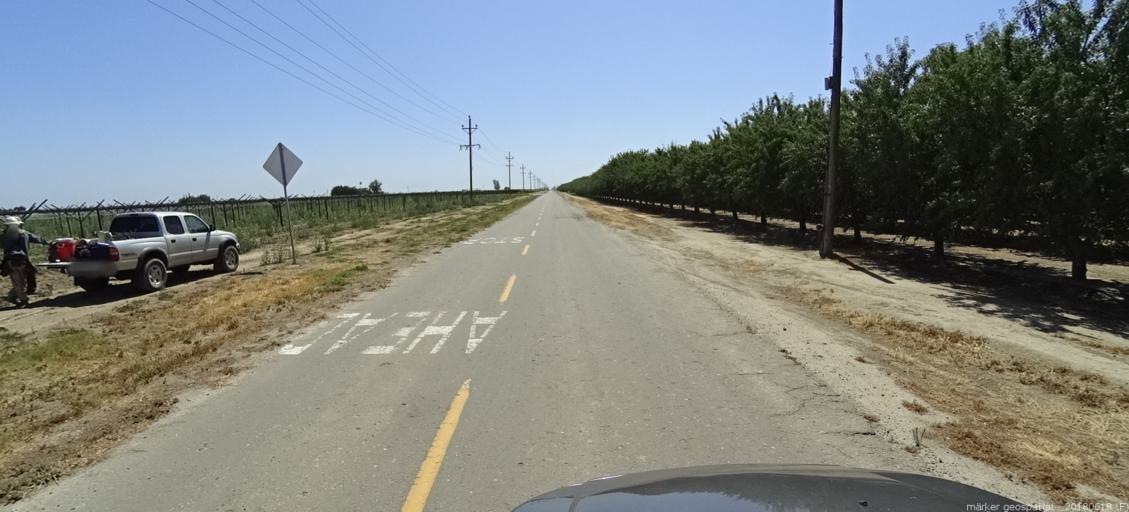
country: US
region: California
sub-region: Madera County
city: Parkwood
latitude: 36.8803
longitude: -120.1631
